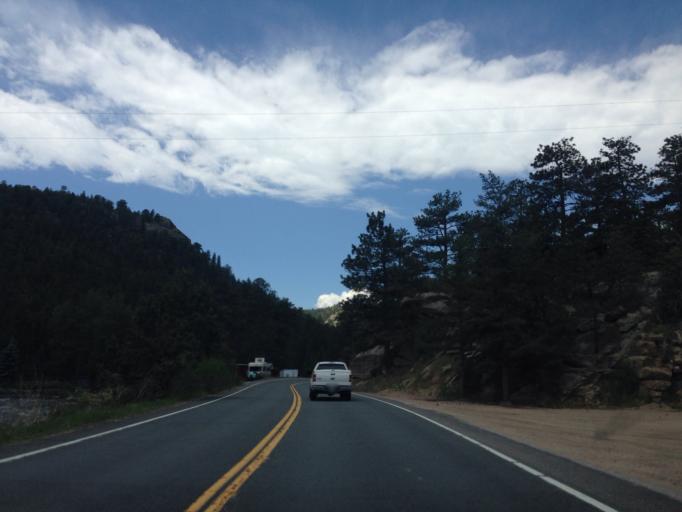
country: US
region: Colorado
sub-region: Larimer County
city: Estes Park
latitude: 40.3911
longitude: -105.4564
